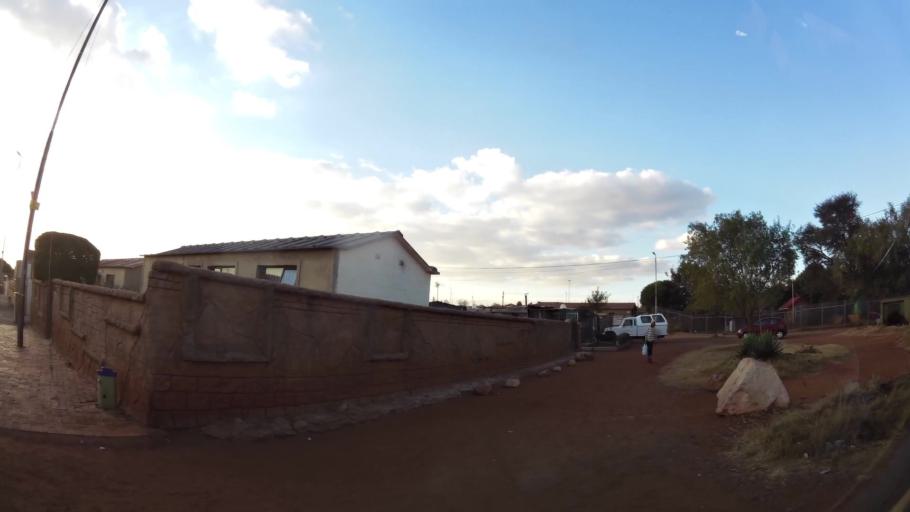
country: ZA
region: Gauteng
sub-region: West Rand District Municipality
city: Krugersdorp
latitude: -26.0779
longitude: 27.7543
